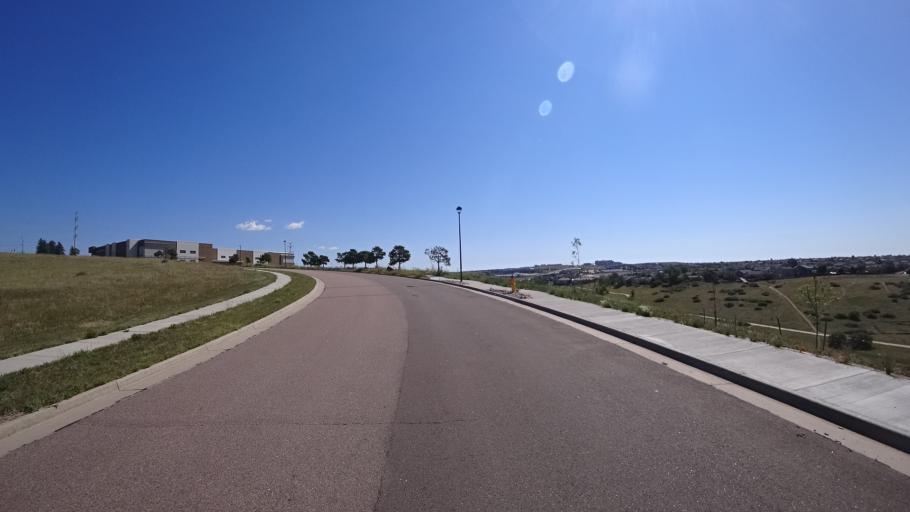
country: US
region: Colorado
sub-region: El Paso County
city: Black Forest
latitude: 38.9380
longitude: -104.7485
